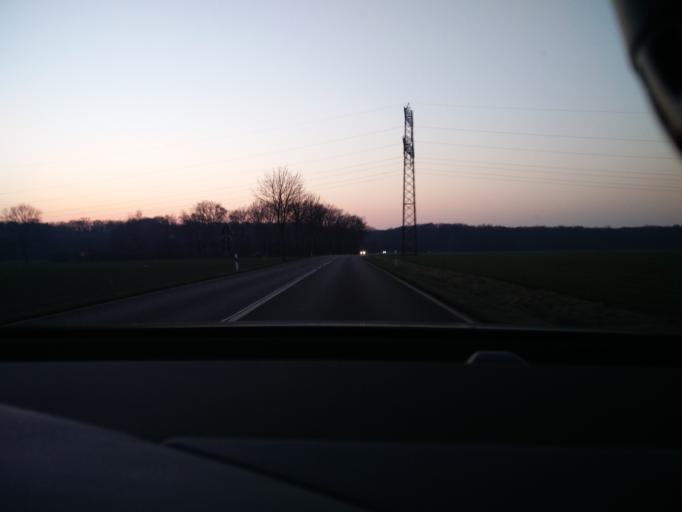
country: DE
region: Lower Saxony
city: Sehnde
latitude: 52.3142
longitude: 9.9043
